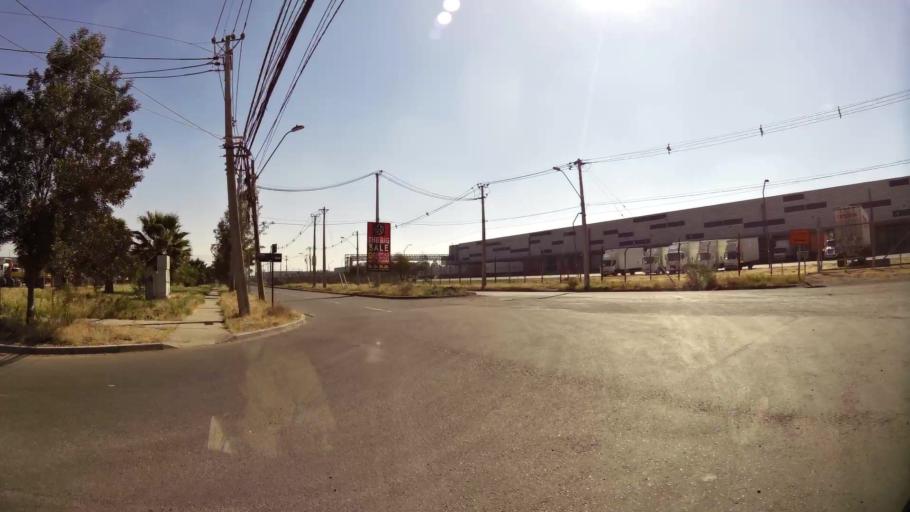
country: CL
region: Santiago Metropolitan
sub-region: Provincia de Chacabuco
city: Chicureo Abajo
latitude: -33.3292
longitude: -70.7125
